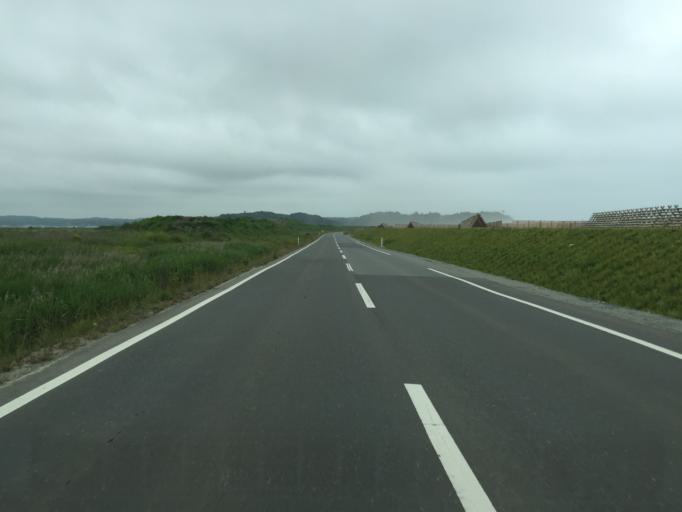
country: JP
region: Fukushima
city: Namie
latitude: 37.7143
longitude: 141.0101
